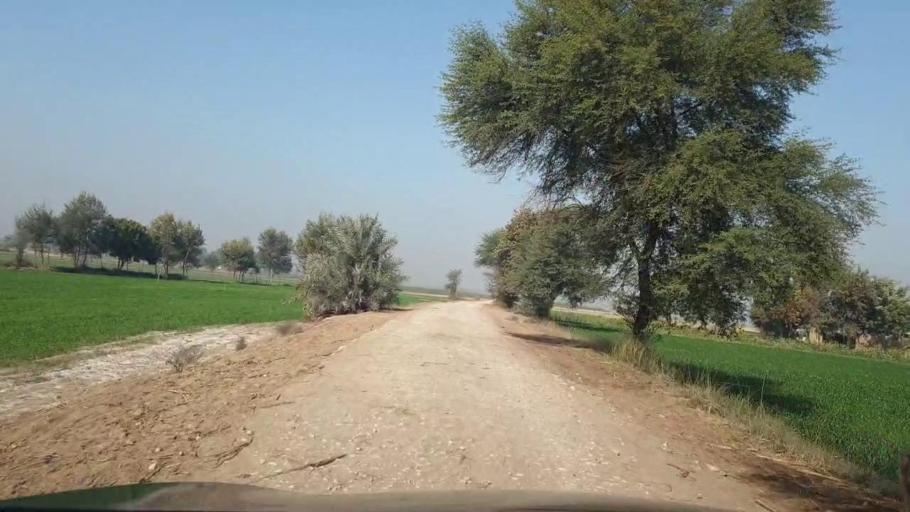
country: PK
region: Sindh
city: Ubauro
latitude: 28.1237
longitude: 69.7501
